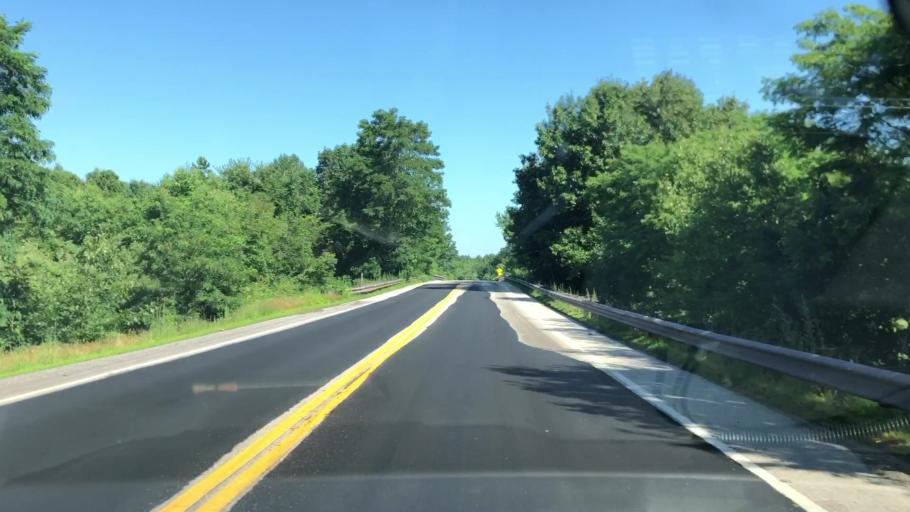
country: US
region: New Hampshire
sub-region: Hillsborough County
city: Milford
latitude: 42.8284
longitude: -71.6088
